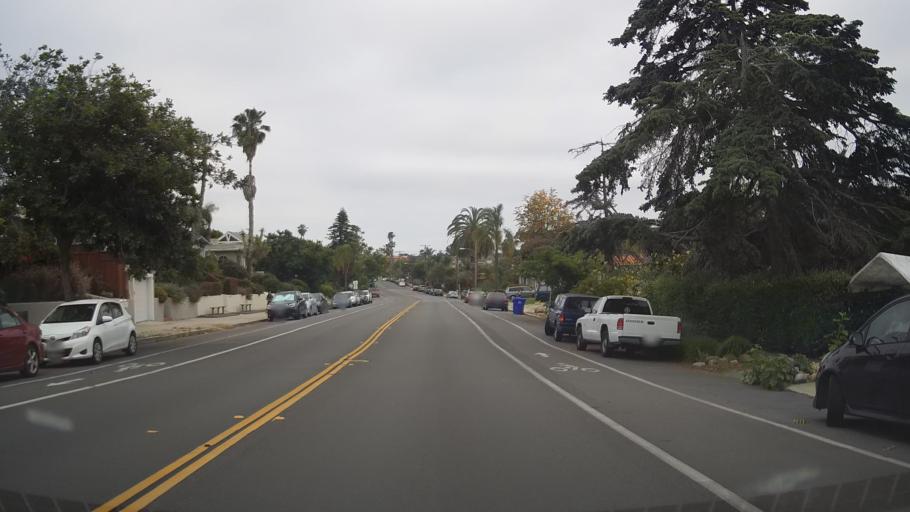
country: US
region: California
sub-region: San Diego County
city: San Diego
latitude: 32.7565
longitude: -117.1513
